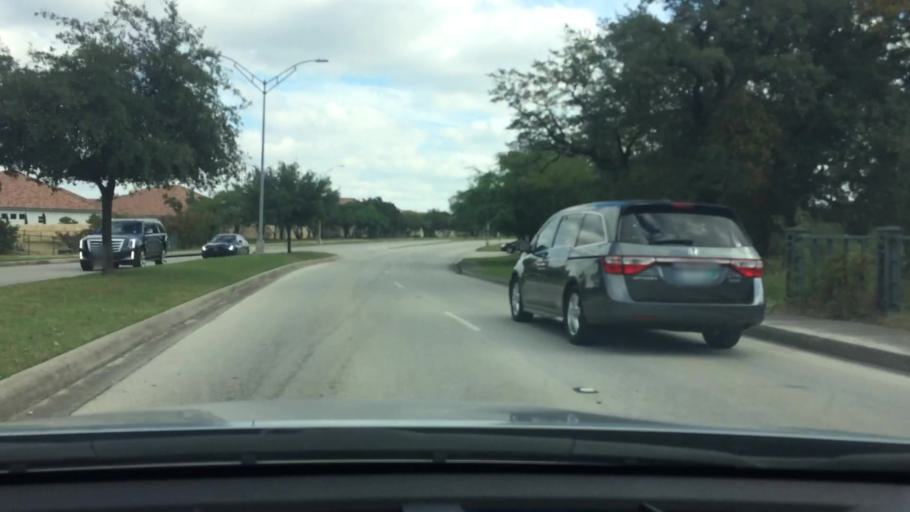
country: US
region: Texas
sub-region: Bexar County
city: Shavano Park
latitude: 29.5903
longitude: -98.5742
